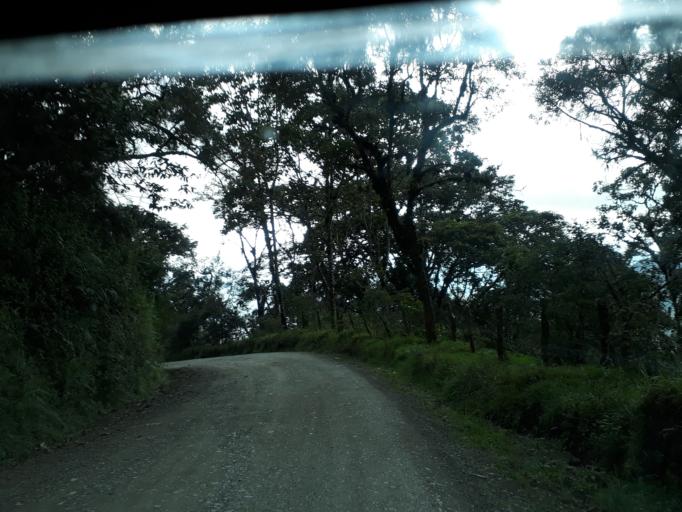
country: CO
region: Cundinamarca
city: Pacho
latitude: 5.2393
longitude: -74.1881
